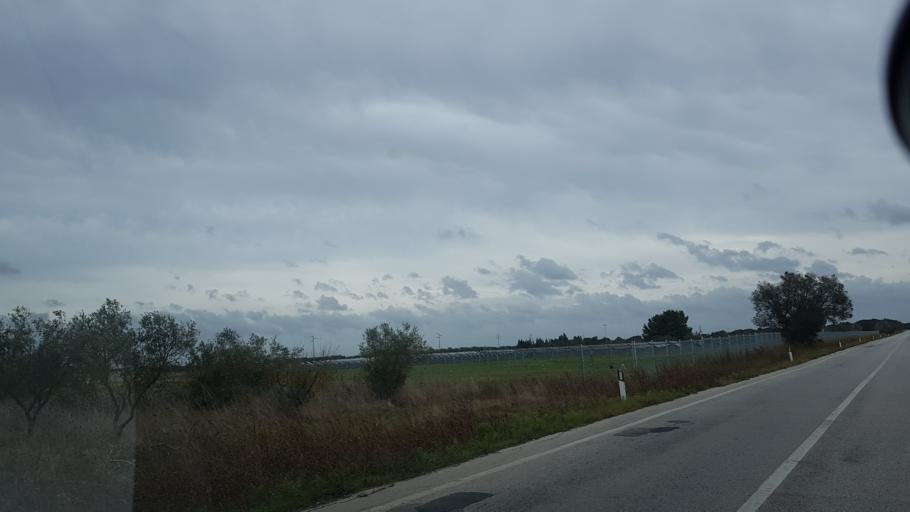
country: IT
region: Apulia
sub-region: Provincia di Lecce
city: Guagnano
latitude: 40.4005
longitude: 17.9142
